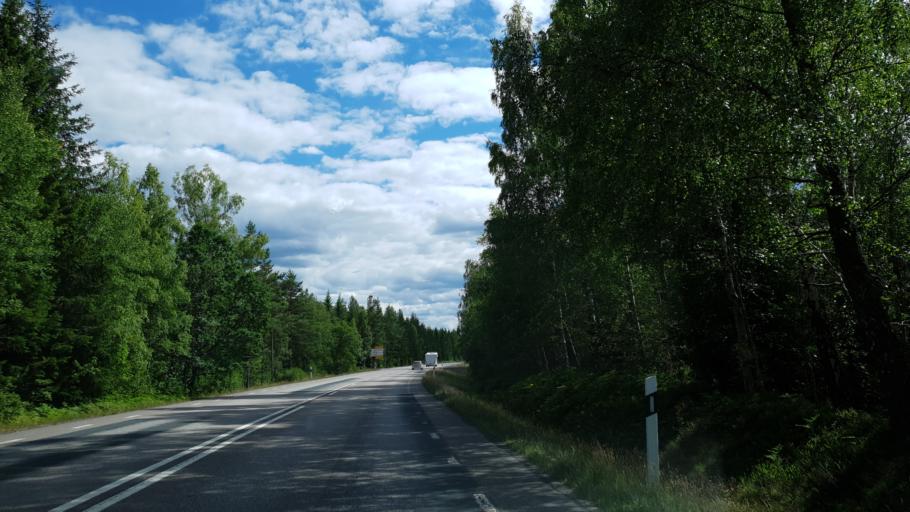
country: SE
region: Kronoberg
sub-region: Uppvidinge Kommun
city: Lenhovda
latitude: 56.8726
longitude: 15.3857
